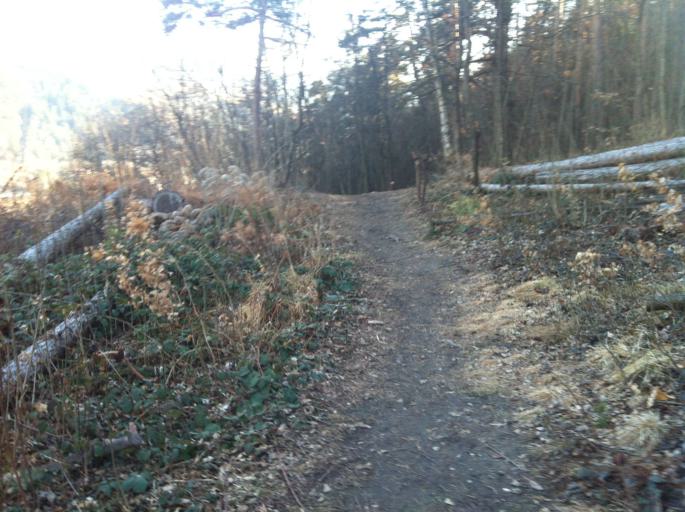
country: IT
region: Trentino-Alto Adige
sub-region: Bolzano
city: Bressanone
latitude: 46.7206
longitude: 11.6669
